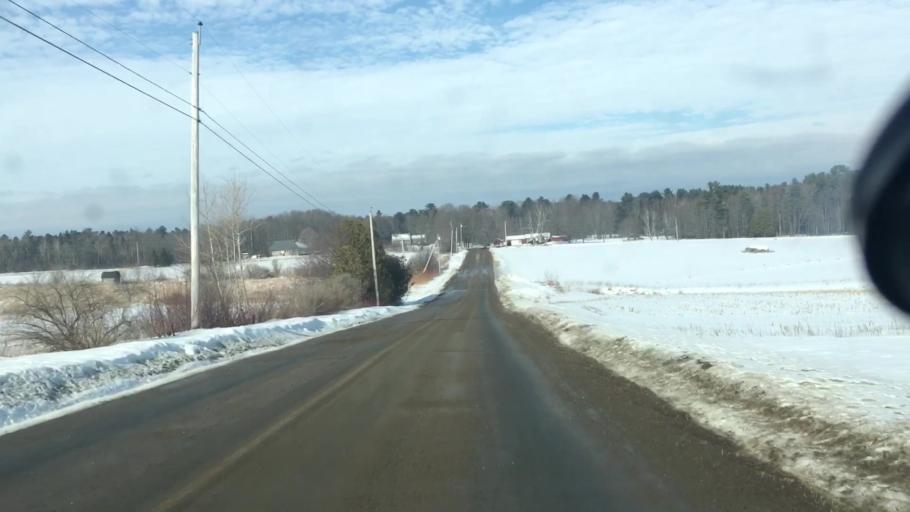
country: US
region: Maine
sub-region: Penobscot County
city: Levant
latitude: 44.8590
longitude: -68.8788
